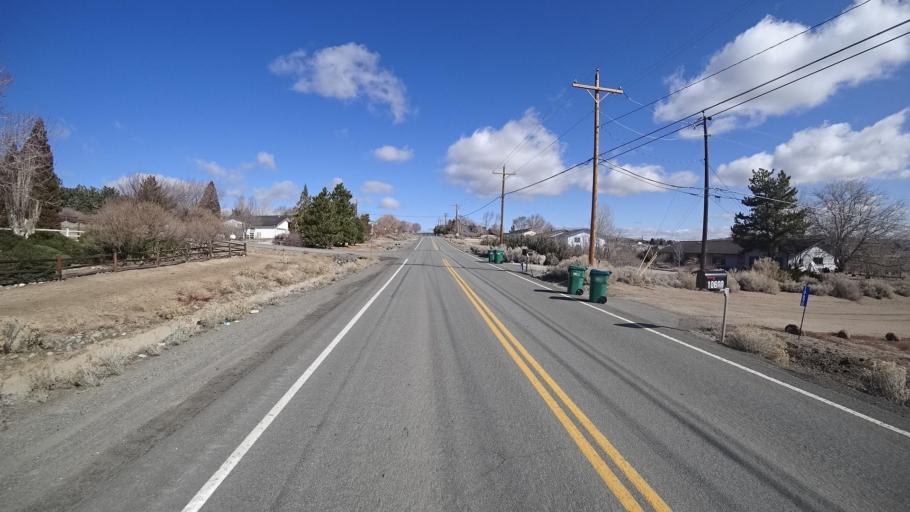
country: US
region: Nevada
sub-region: Washoe County
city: Cold Springs
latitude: 39.6605
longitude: -119.9225
